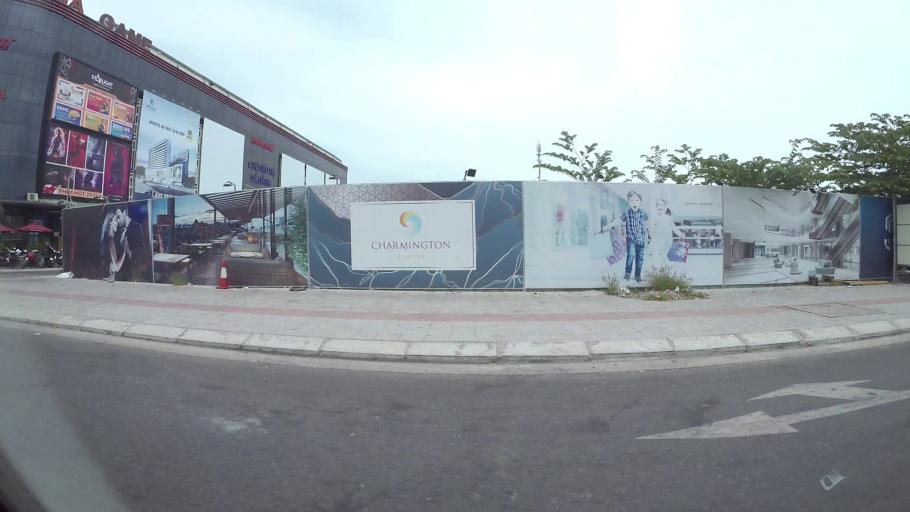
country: VN
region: Da Nang
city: Thanh Khe
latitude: 16.0660
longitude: 108.2037
